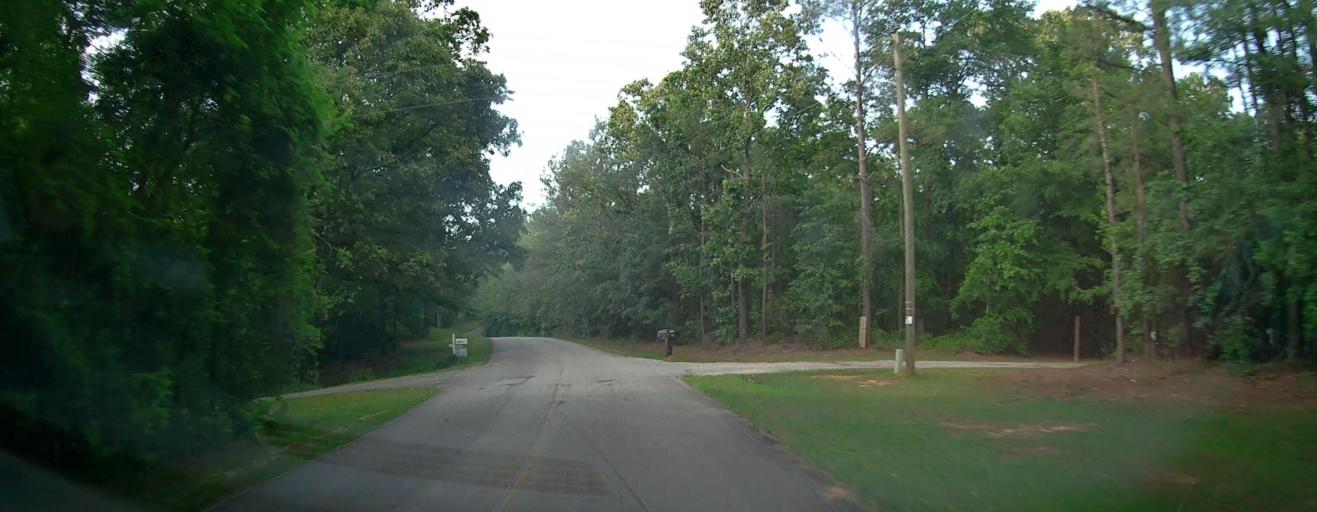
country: US
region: Georgia
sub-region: Peach County
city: Byron
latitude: 32.6143
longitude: -83.7734
